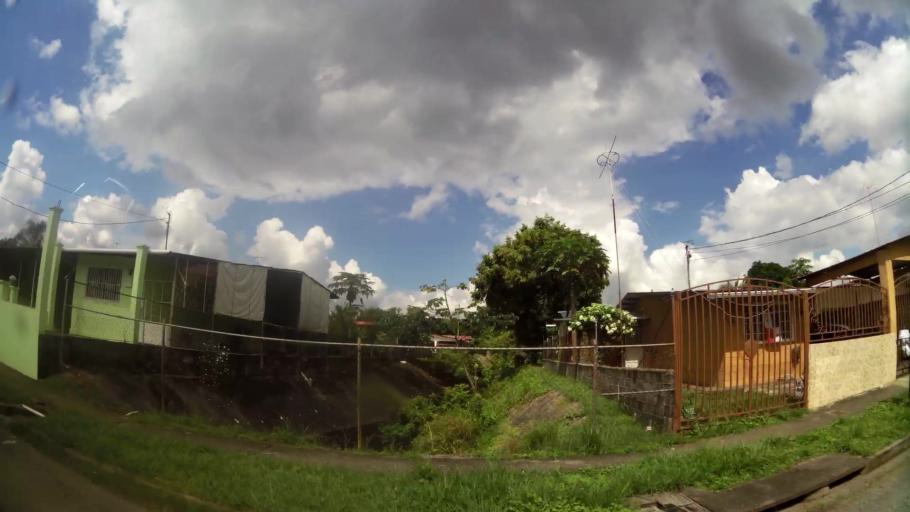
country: PA
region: Panama
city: Nuevo Arraijan
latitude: 8.9325
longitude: -79.7362
